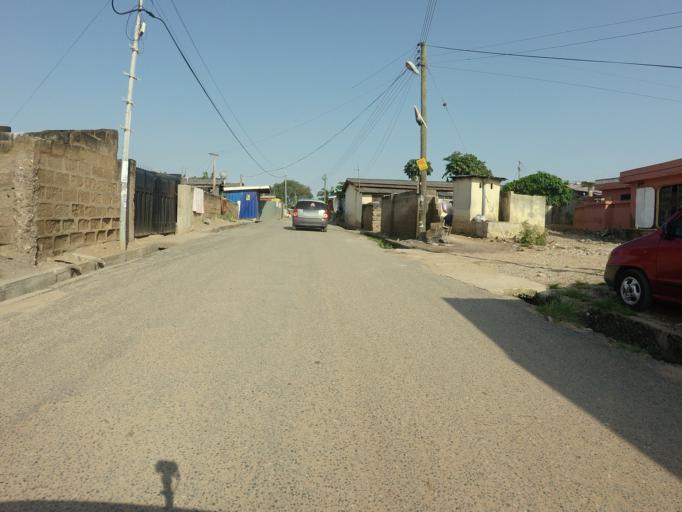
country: GH
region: Greater Accra
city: Dome
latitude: 5.6125
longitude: -0.2426
